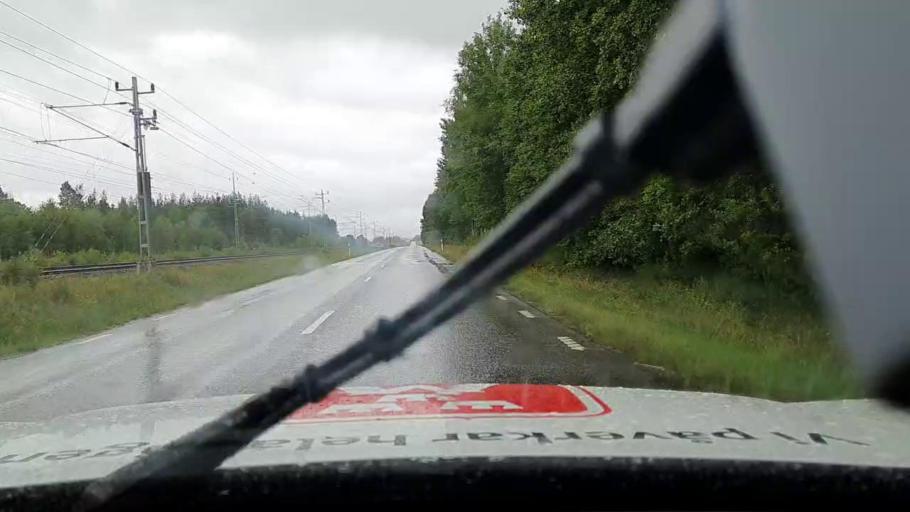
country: SE
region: Vaestra Goetaland
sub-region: Toreboda Kommun
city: Toereboda
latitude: 58.6620
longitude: 14.0886
